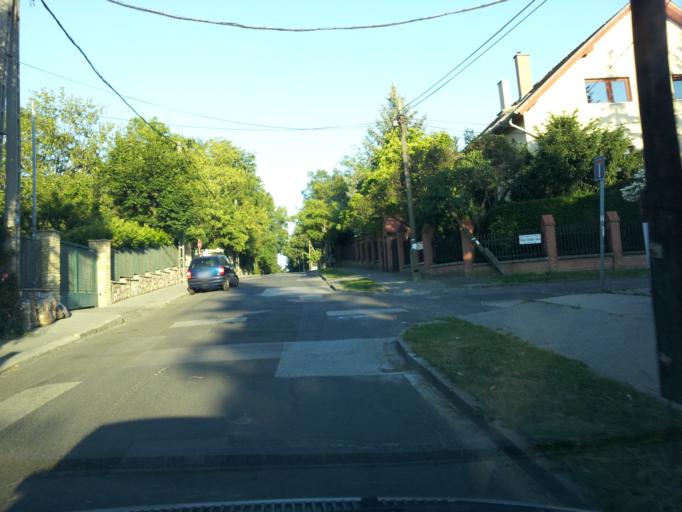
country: HU
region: Budapest
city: Budapest XII. keruelet
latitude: 47.5157
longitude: 18.9931
